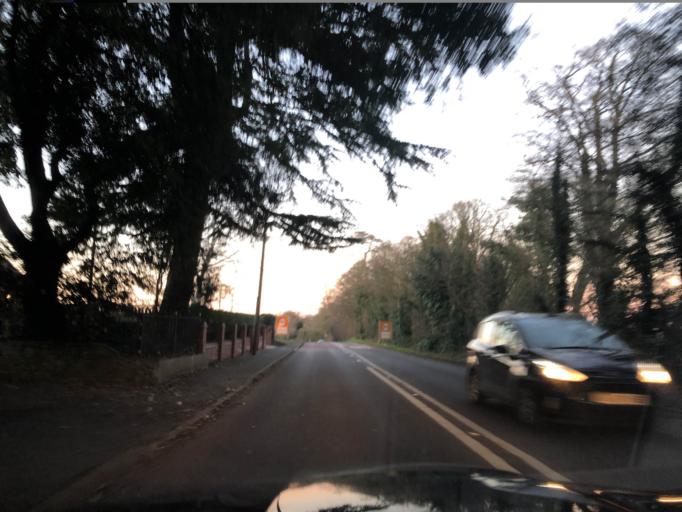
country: GB
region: England
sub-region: Warwickshire
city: Kenilworth
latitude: 52.3204
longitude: -1.5760
